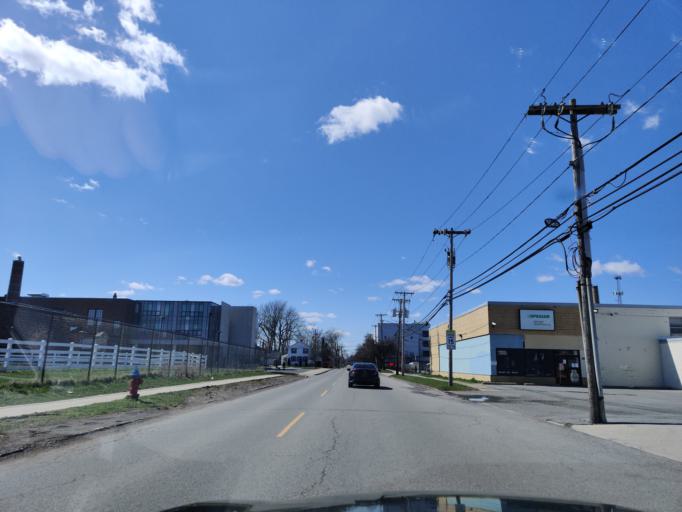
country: US
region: New York
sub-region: Erie County
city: Kenmore
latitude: 42.9420
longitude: -78.8705
